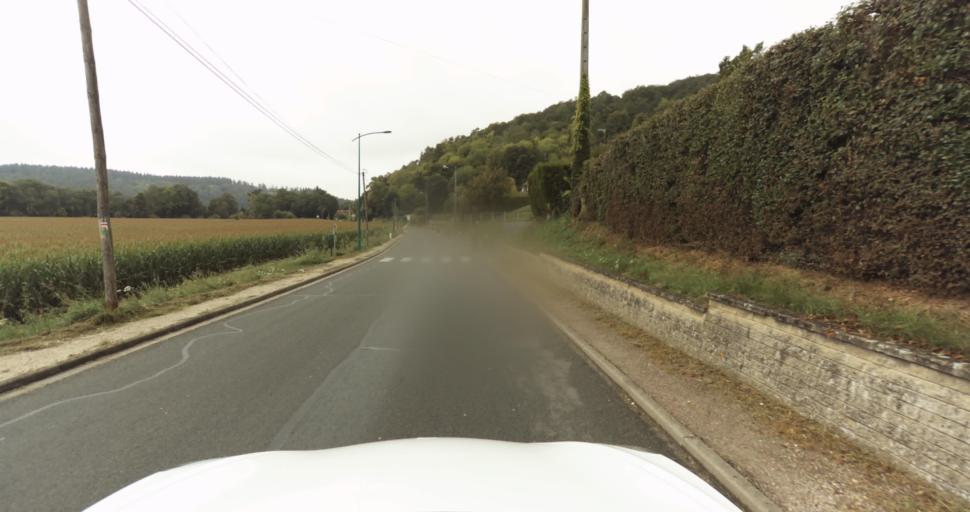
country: FR
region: Haute-Normandie
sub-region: Departement de l'Eure
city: Normanville
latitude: 49.0805
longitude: 1.1560
